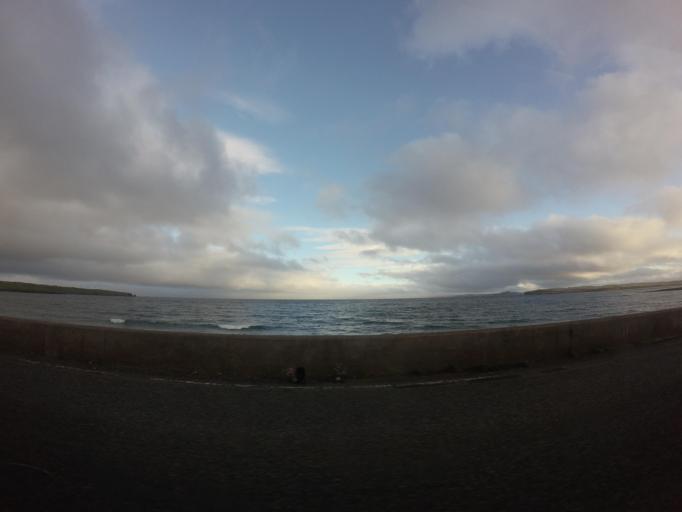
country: GB
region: Scotland
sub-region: Eilean Siar
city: Stornoway
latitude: 58.2059
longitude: -6.3033
